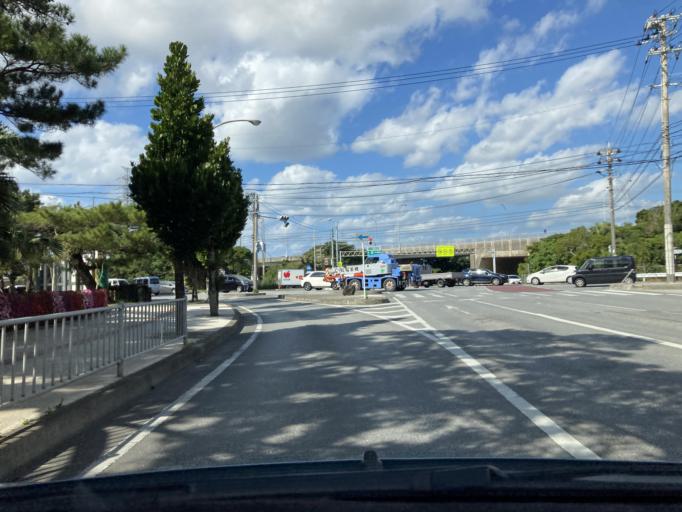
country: JP
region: Okinawa
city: Okinawa
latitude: 26.3347
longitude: 127.7891
